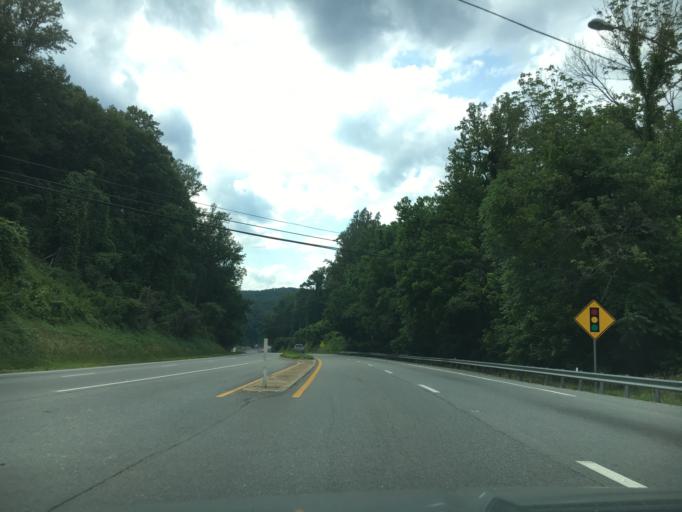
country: US
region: Virginia
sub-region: Roanoke County
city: Narrows
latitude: 37.1116
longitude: -79.9480
